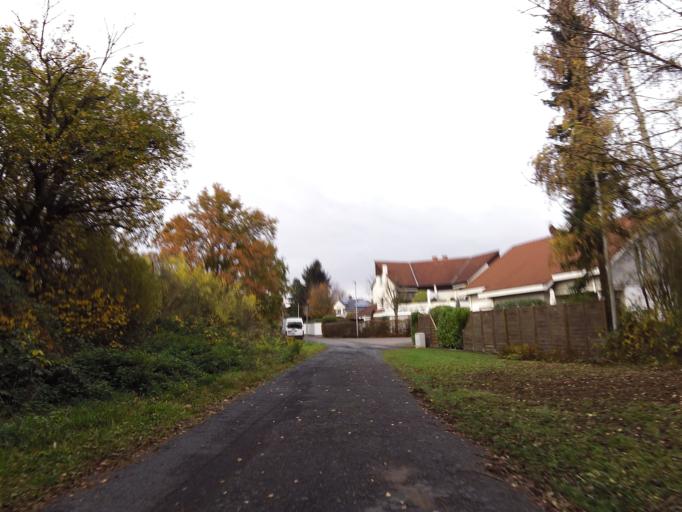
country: DE
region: Hesse
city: Morfelden-Walldorf
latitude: 49.9930
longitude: 8.5891
